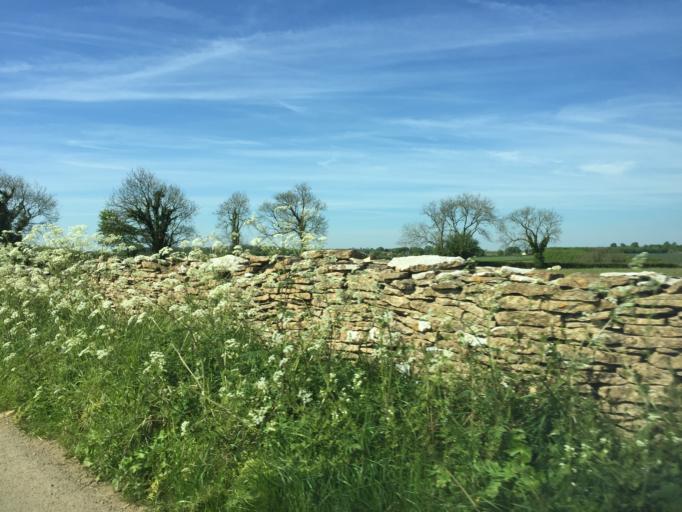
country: GB
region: England
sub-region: Wiltshire
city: Luckington
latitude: 51.6126
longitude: -2.2588
